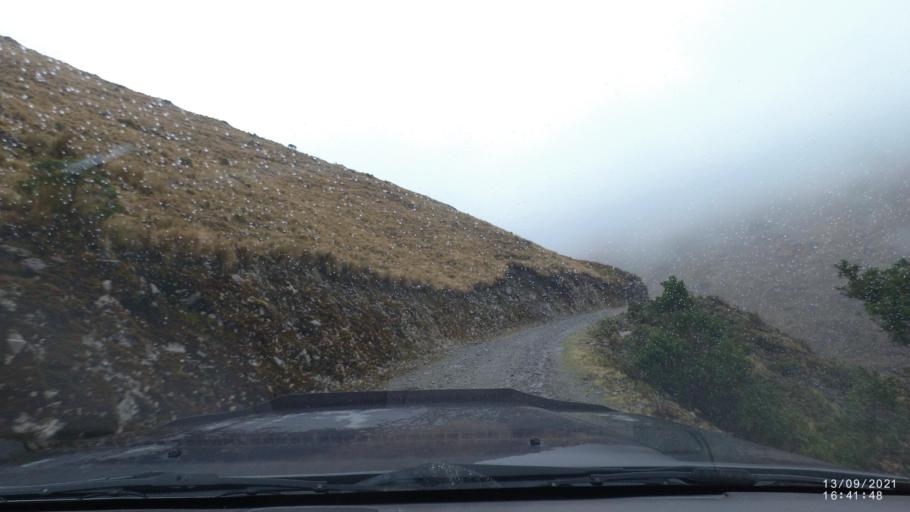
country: BO
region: Cochabamba
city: Colomi
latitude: -17.2851
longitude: -65.7114
